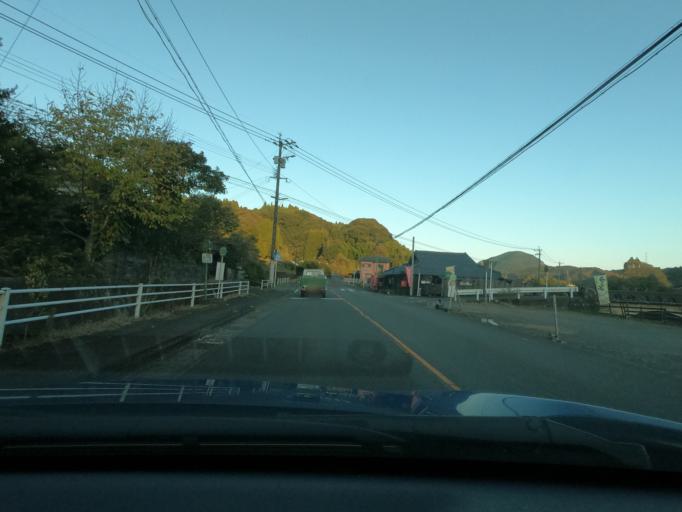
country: JP
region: Kagoshima
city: Satsumasendai
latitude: 31.7920
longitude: 130.4549
